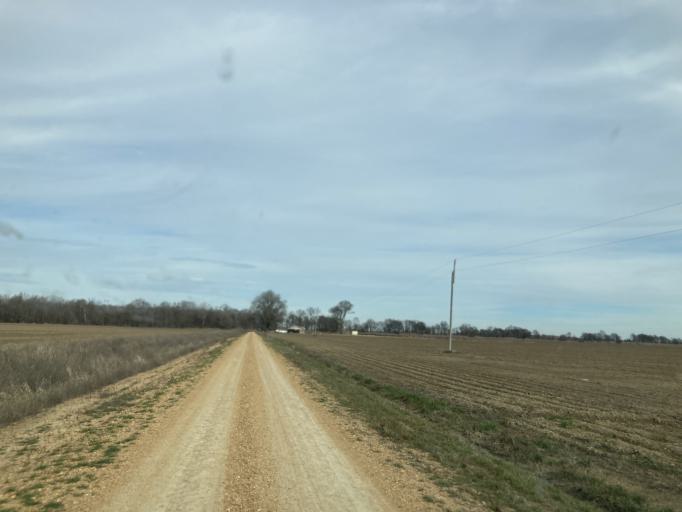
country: US
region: Mississippi
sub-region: Humphreys County
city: Belzoni
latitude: 33.0634
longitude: -90.6577
